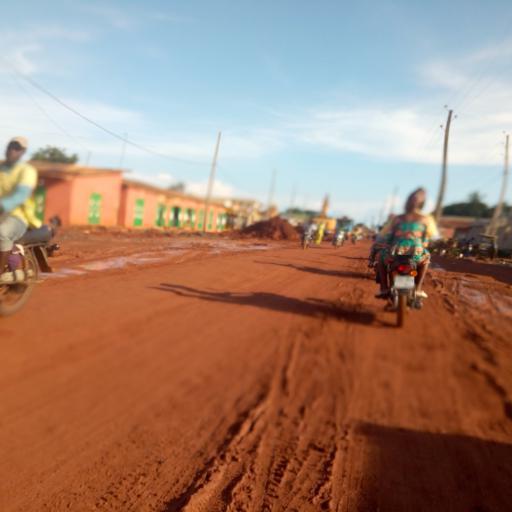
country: BJ
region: Atlantique
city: Hevie
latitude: 6.4034
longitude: 2.2676
